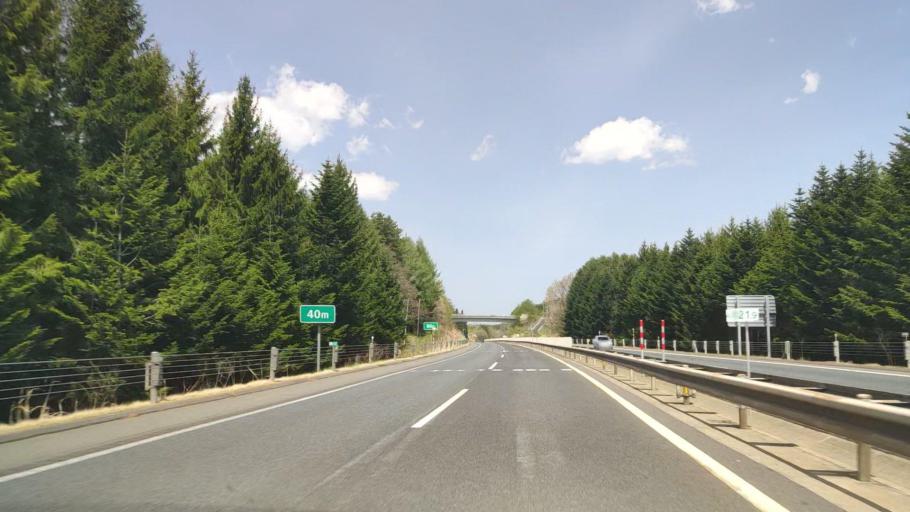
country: JP
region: Aomori
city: Hachinohe
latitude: 40.4134
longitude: 141.4432
